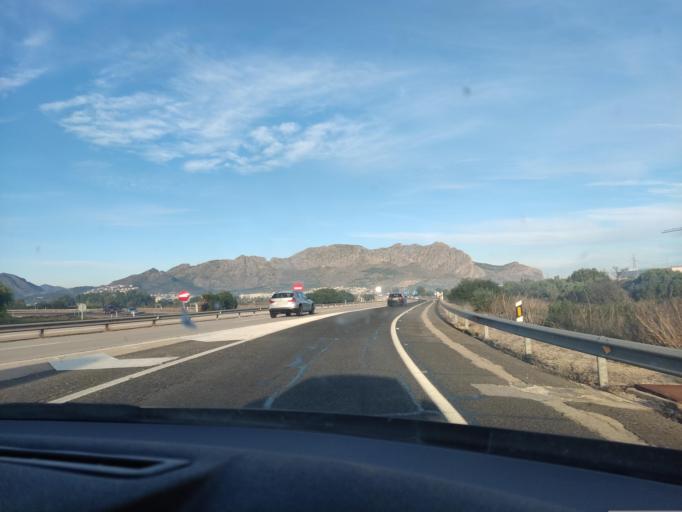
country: ES
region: Valencia
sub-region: Provincia de Alicante
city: Ondara
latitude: 38.8145
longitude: 0.0209
